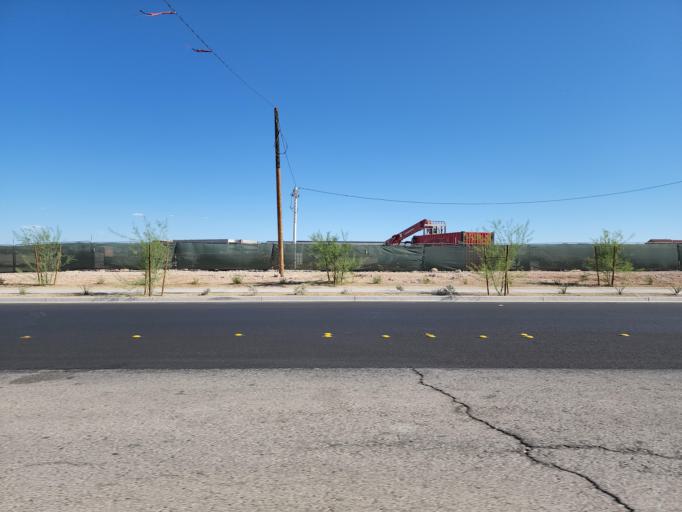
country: US
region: Nevada
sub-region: Clark County
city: Spring Valley
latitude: 36.0776
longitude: -115.2639
